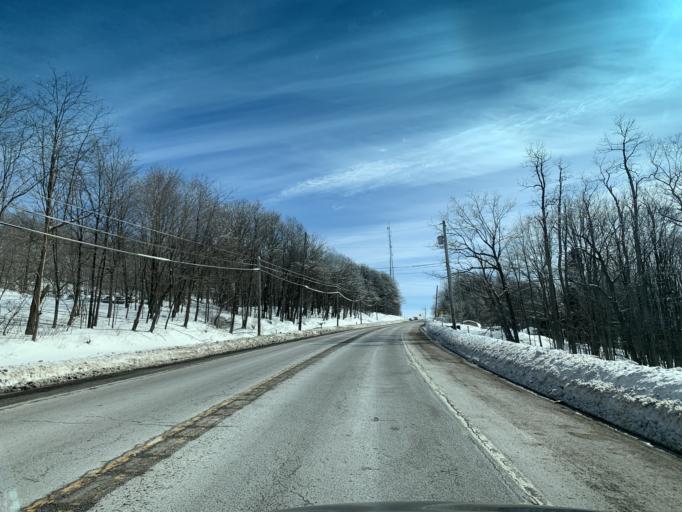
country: US
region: Maryland
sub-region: Allegany County
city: Frostburg
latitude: 39.6792
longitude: -78.9627
